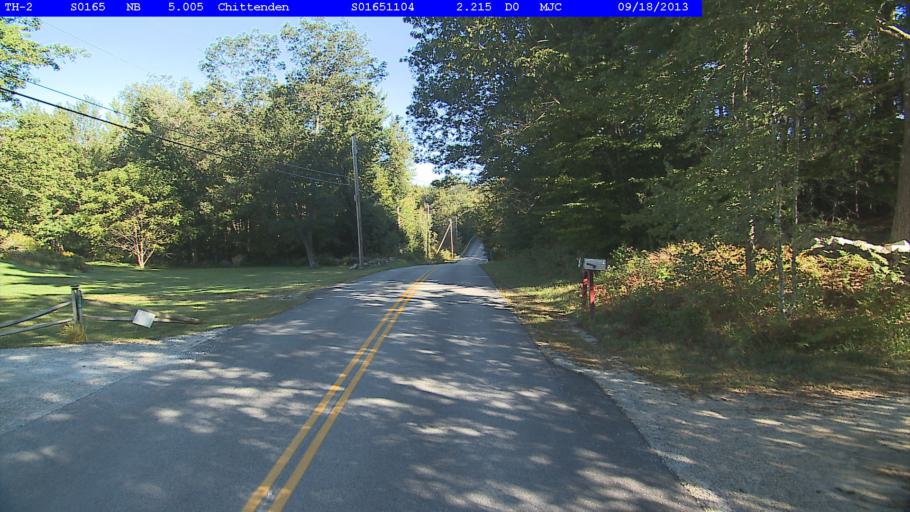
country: US
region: Vermont
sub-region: Rutland County
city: Rutland
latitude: 43.7075
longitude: -72.9615
